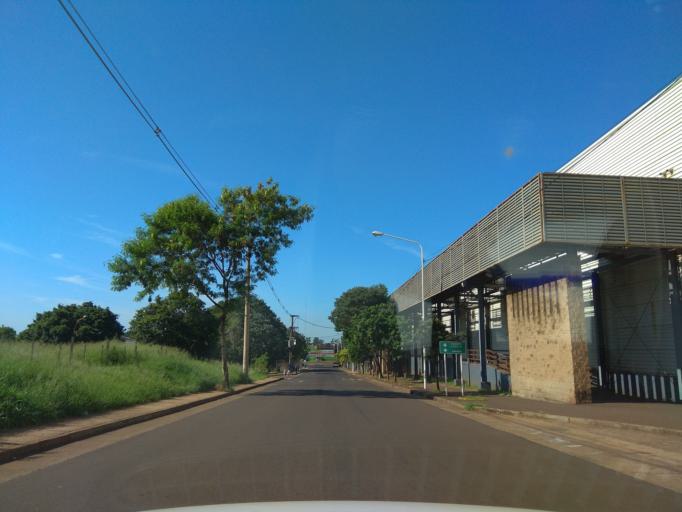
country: AR
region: Misiones
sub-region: Departamento de Capital
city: Posadas
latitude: -27.4002
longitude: -55.9157
